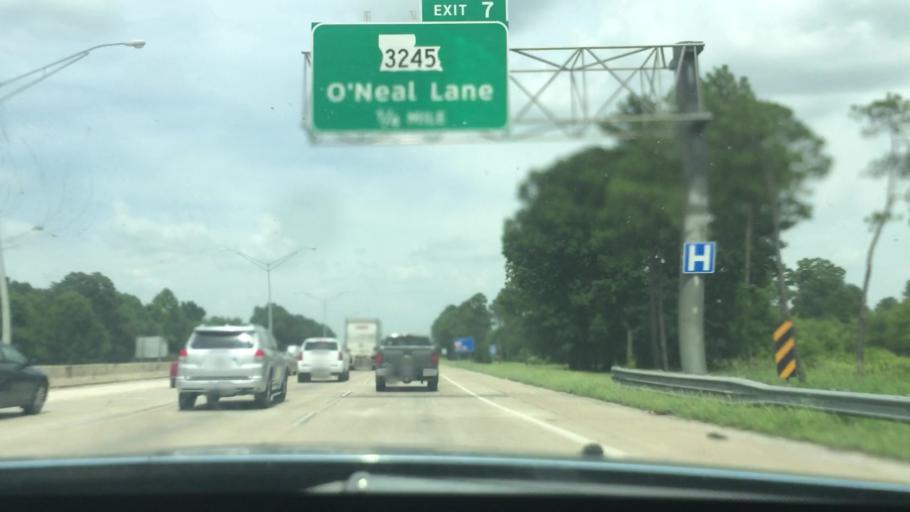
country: US
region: Louisiana
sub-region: East Baton Rouge Parish
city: Shenandoah
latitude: 30.4399
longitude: -91.0171
